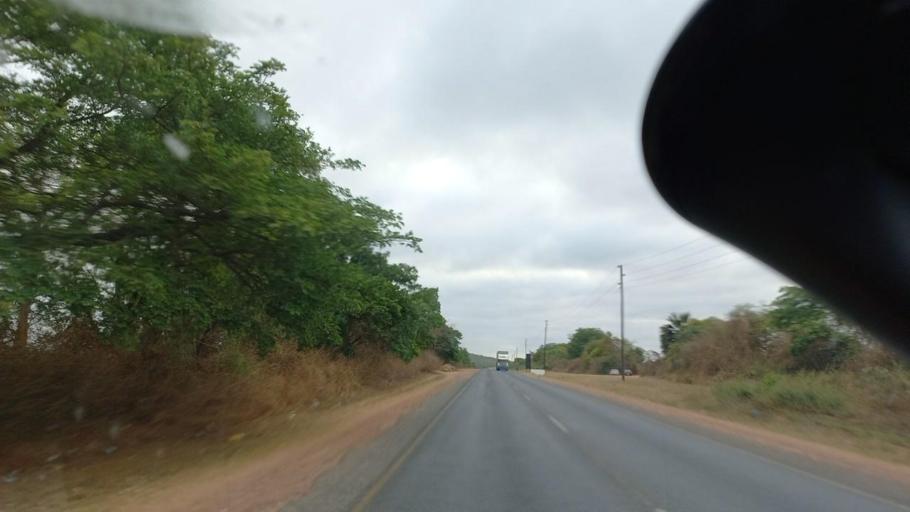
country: ZM
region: Lusaka
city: Chongwe
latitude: -15.3458
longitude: 28.5842
